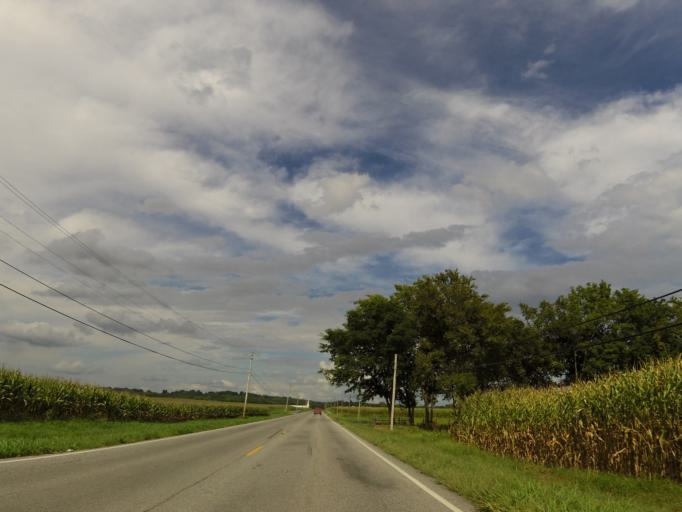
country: US
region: Kentucky
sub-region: Christian County
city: Hopkinsville
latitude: 36.8738
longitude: -87.5287
